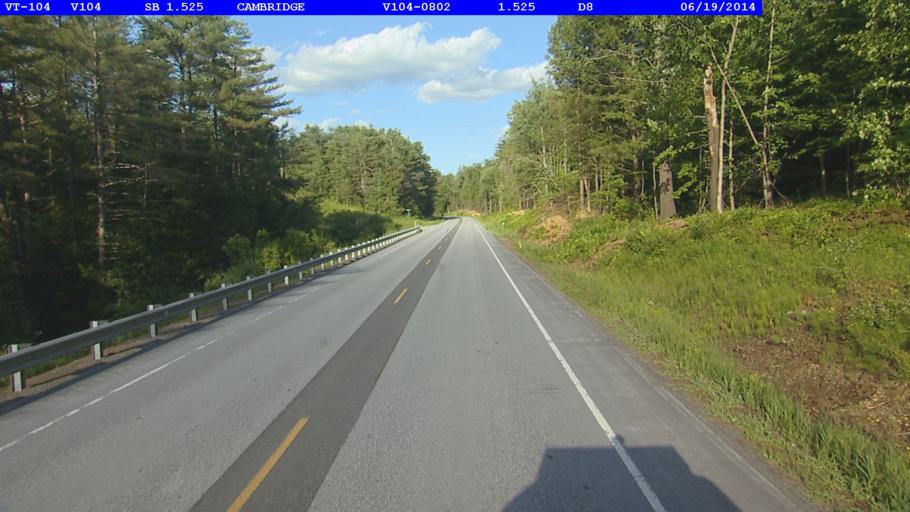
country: US
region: Vermont
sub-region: Chittenden County
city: Jericho
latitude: 44.6411
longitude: -72.9171
